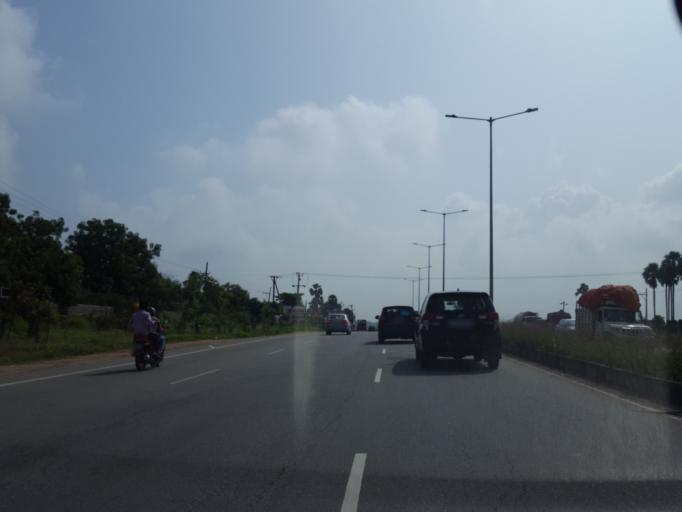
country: IN
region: Telangana
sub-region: Rangareddi
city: Ghatkesar
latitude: 17.3067
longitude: 78.7172
